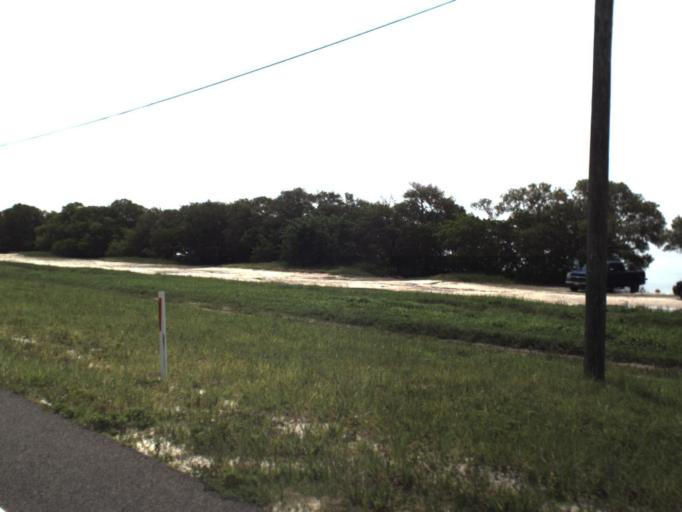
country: US
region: Florida
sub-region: Pinellas County
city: Gandy
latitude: 27.8730
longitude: -82.6055
